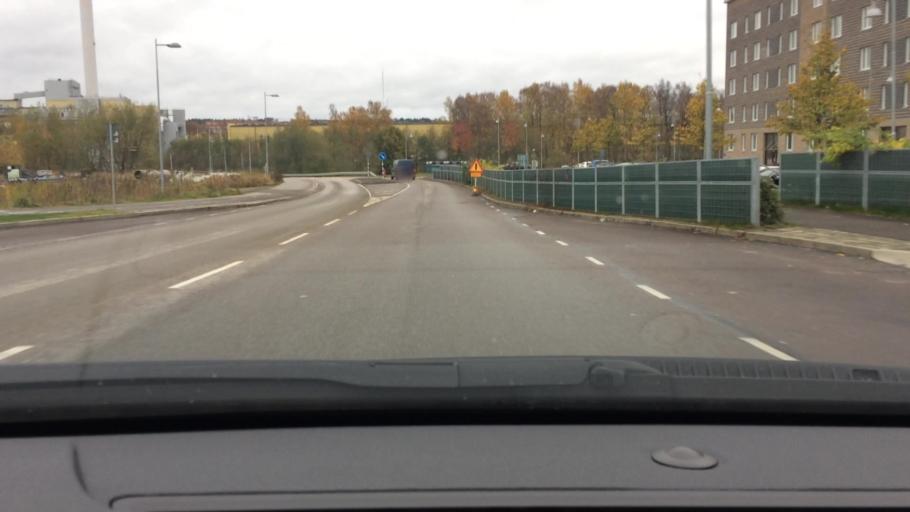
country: SE
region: Vaestra Goetaland
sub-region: Goteborg
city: Eriksbo
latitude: 57.7333
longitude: 12.0301
